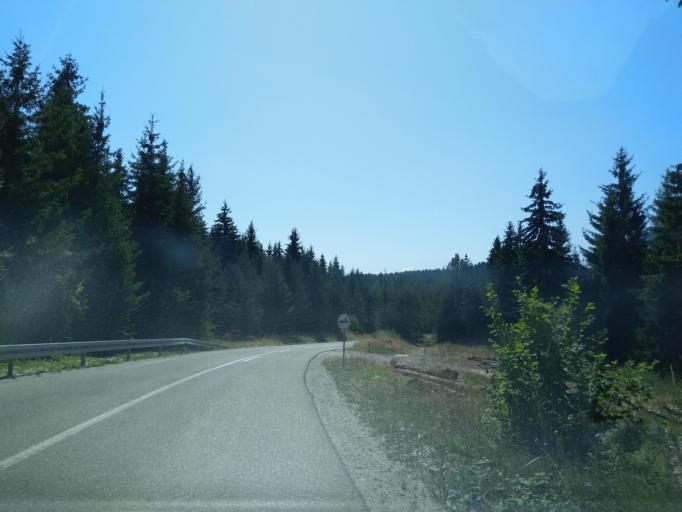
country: RS
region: Central Serbia
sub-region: Zlatiborski Okrug
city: Nova Varos
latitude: 43.3626
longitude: 19.8540
